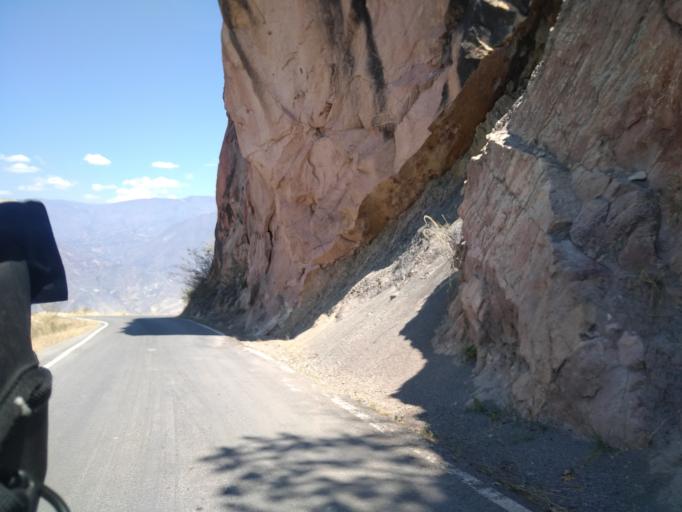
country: PE
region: Amazonas
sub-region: Provincia de Chachapoyas
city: Balsas
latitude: -6.8509
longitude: -77.9814
